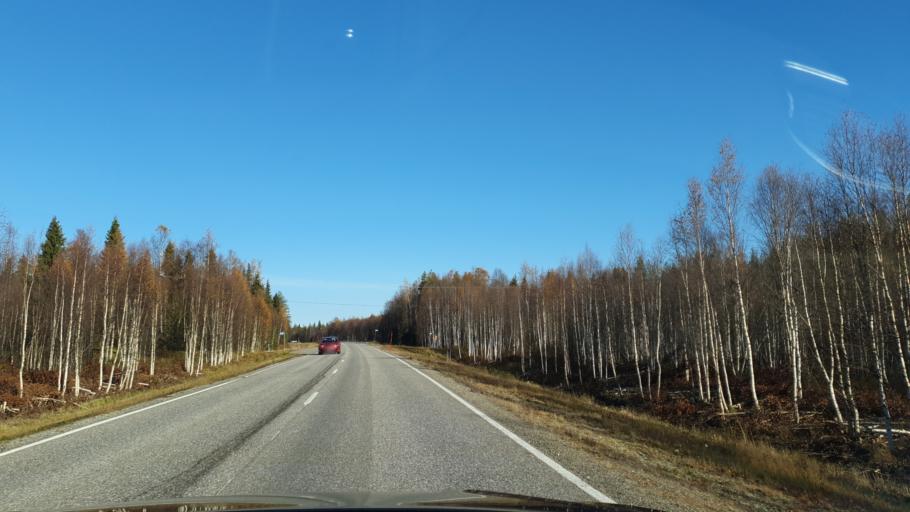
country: FI
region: Lapland
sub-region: Tunturi-Lappi
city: Kittilae
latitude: 67.3866
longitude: 24.9106
